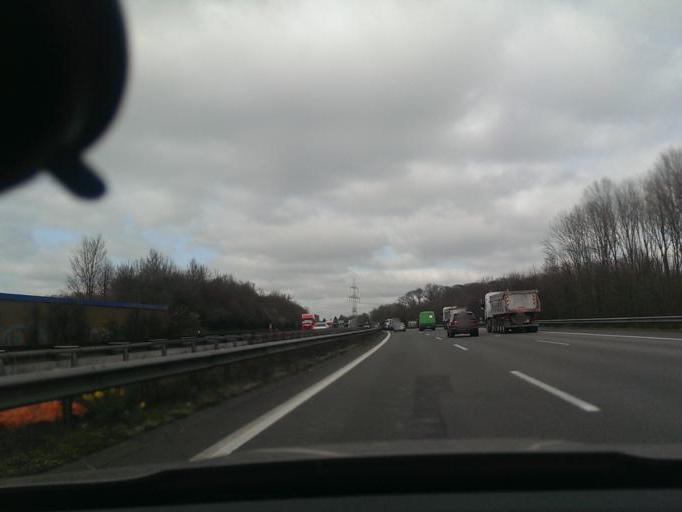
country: DE
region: North Rhine-Westphalia
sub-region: Regierungsbezirk Detmold
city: Leopoldshohe
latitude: 52.0394
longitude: 8.6466
